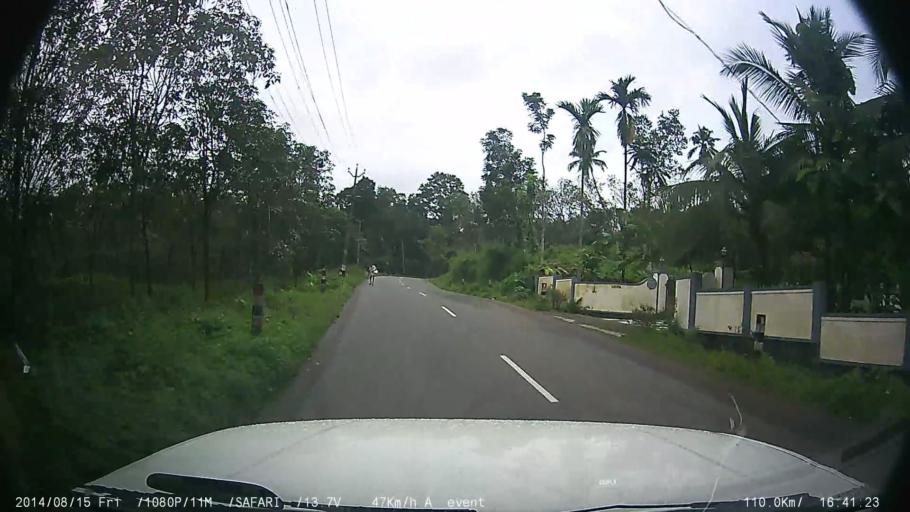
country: IN
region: Kerala
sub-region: Kottayam
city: Palackattumala
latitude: 9.7576
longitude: 76.5832
